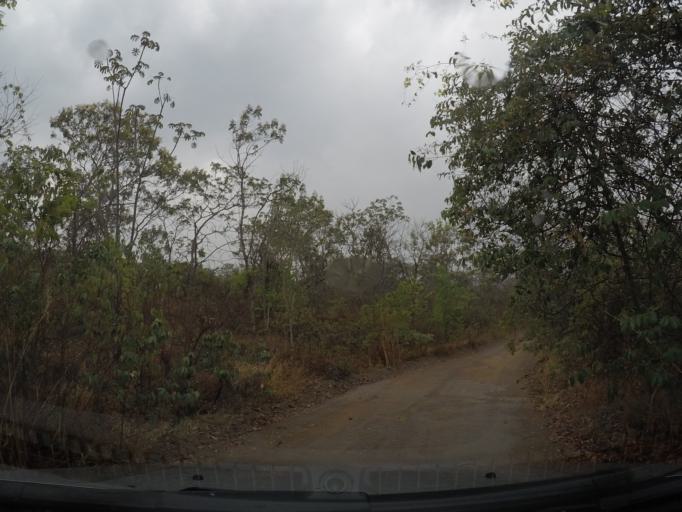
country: BR
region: Goias
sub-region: Pirenopolis
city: Pirenopolis
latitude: -15.8272
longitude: -48.8837
